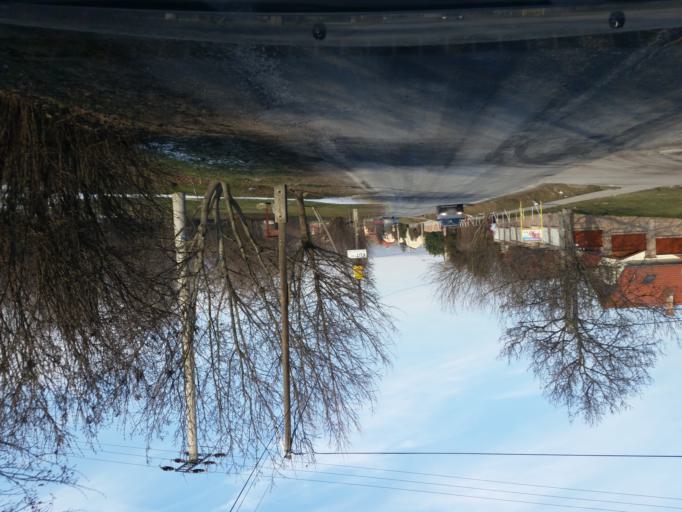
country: HU
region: Pest
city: Paty
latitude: 47.5182
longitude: 18.8325
